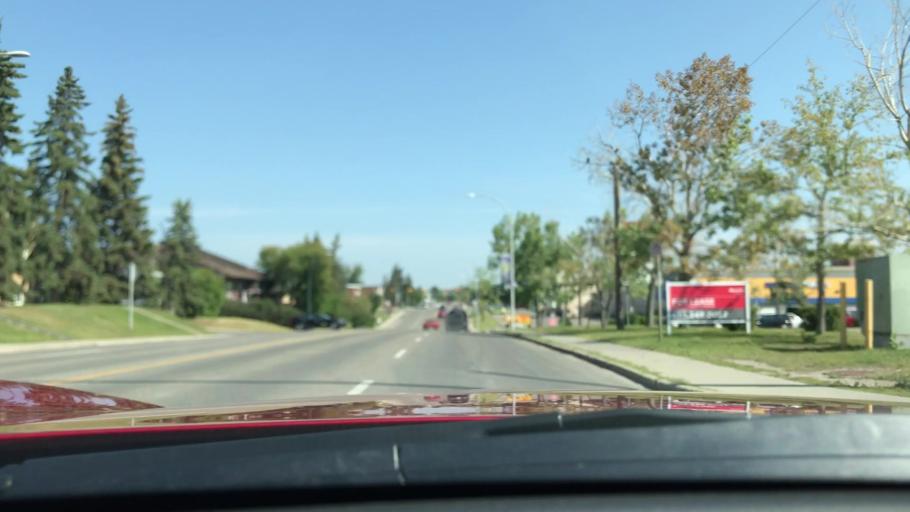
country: CA
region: Alberta
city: Calgary
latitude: 51.0390
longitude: -114.1412
